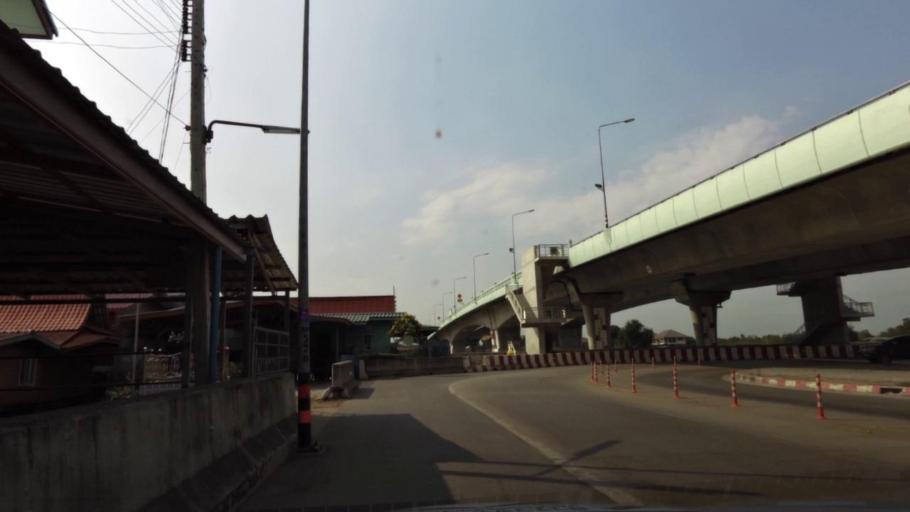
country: TH
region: Phra Nakhon Si Ayutthaya
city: Phra Nakhon Si Ayutthaya
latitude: 14.3309
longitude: 100.5784
